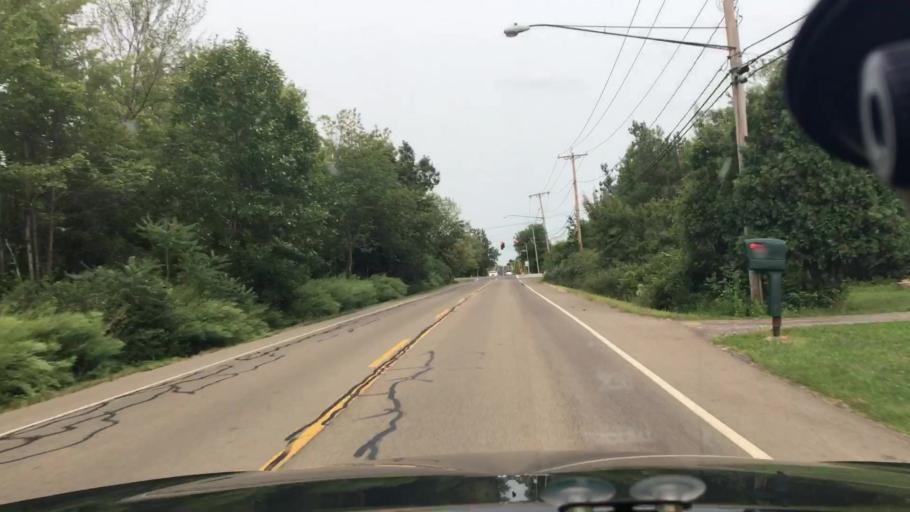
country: US
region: New York
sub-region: Erie County
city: Wanakah
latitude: 42.7074
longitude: -78.9217
